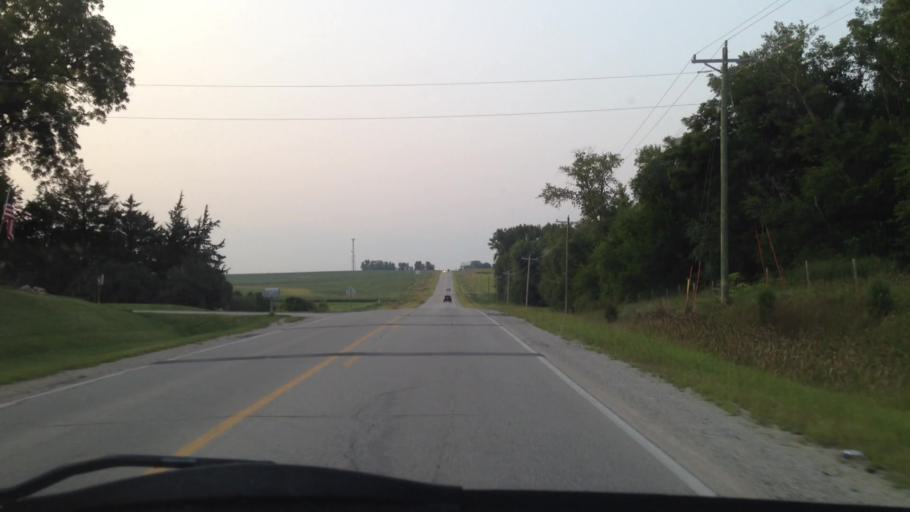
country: US
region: Iowa
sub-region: Benton County
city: Atkins
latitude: 42.0670
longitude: -91.8691
